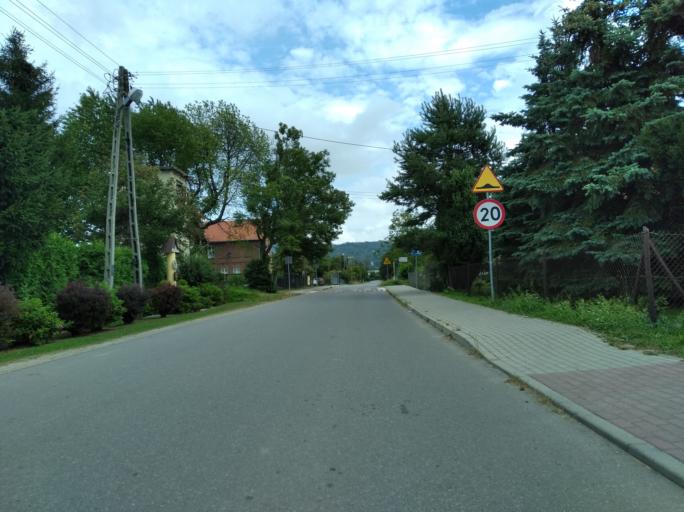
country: PL
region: Subcarpathian Voivodeship
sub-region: Powiat krosnienski
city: Odrzykon
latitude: 49.7398
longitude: 21.7447
